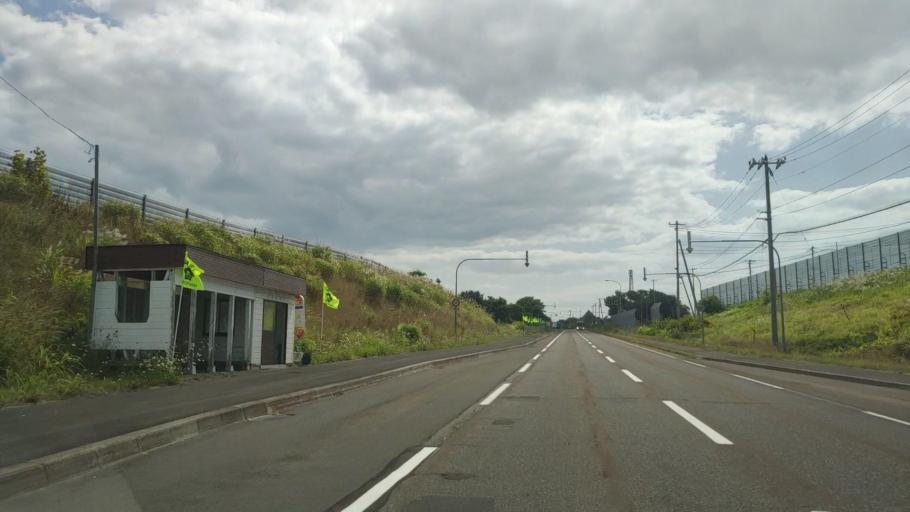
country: JP
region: Hokkaido
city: Rumoi
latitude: 44.5681
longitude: 141.7871
